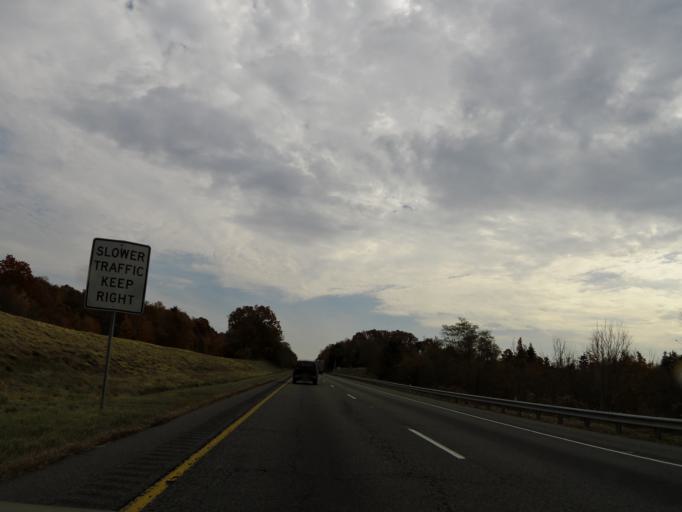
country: US
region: Virginia
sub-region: Carroll County
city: Woodlawn
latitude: 36.8038
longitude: -80.8501
